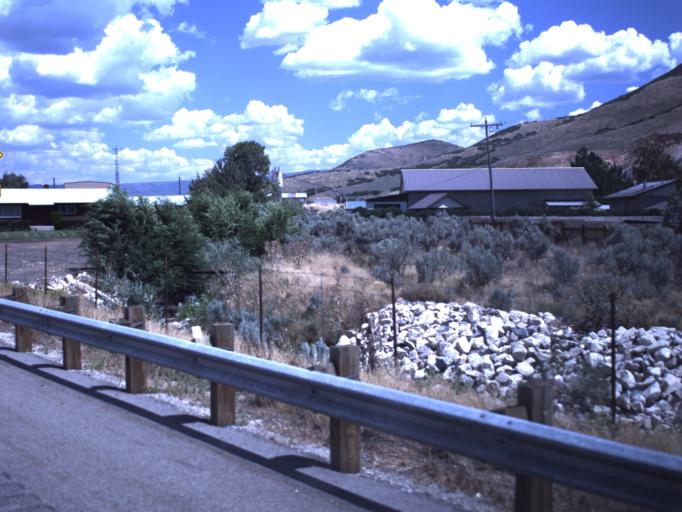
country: US
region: Utah
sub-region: Wasatch County
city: Midway
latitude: 40.4631
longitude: -111.4610
